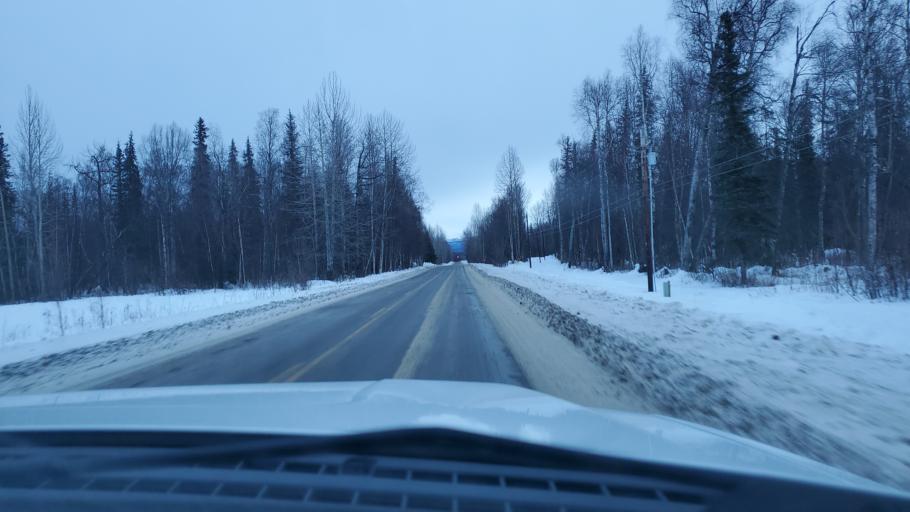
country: US
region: Alaska
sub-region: Matanuska-Susitna Borough
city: Y
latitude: 62.3163
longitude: -150.2508
